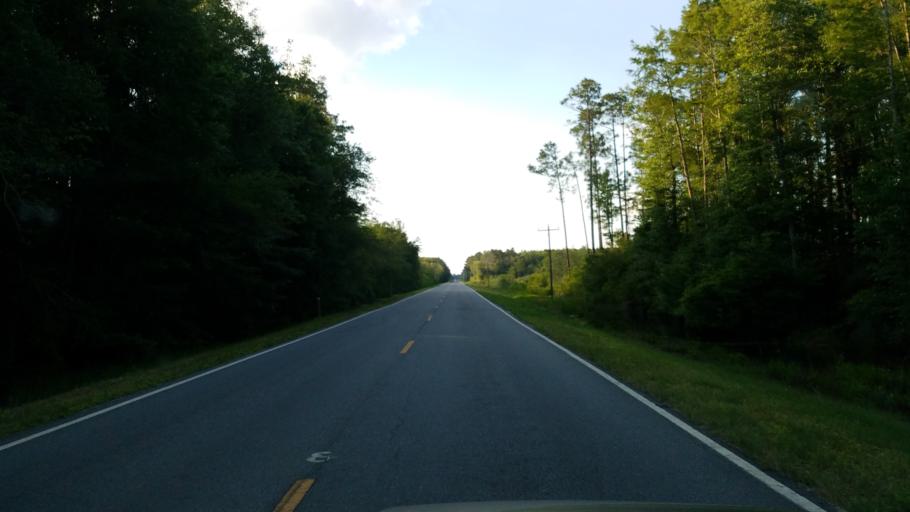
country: US
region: Georgia
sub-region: Lanier County
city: Lakeland
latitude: 31.1089
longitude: -83.0812
